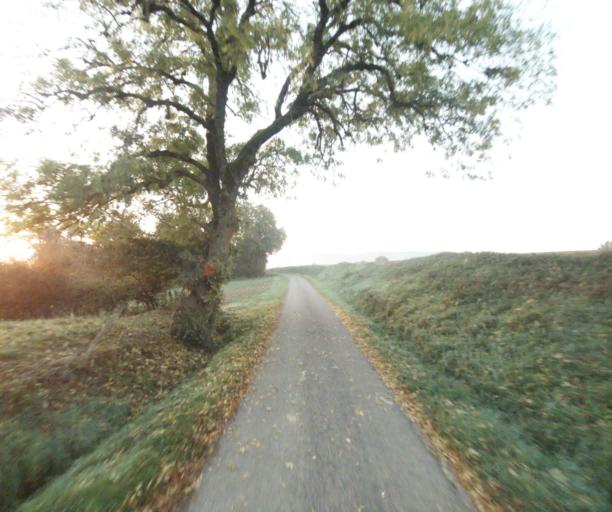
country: FR
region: Midi-Pyrenees
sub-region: Departement du Gers
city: Vic-Fezensac
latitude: 43.7812
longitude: 0.2373
